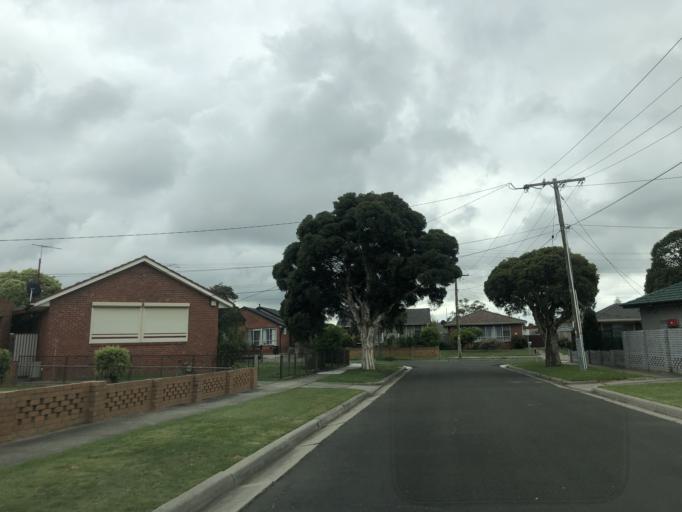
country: AU
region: Victoria
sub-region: Greater Dandenong
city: Dandenong North
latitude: -37.9622
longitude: 145.2074
